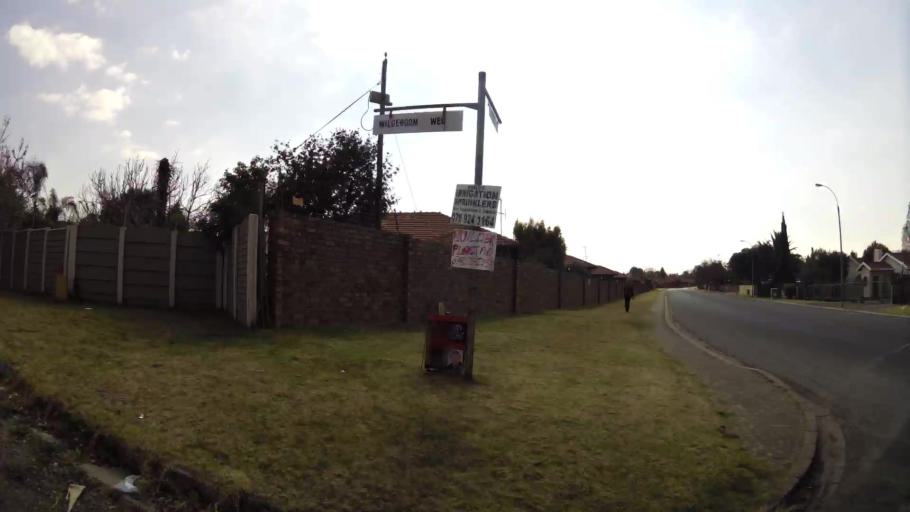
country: ZA
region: Gauteng
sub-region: City of Johannesburg Metropolitan Municipality
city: Modderfontein
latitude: -26.0815
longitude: 28.2335
